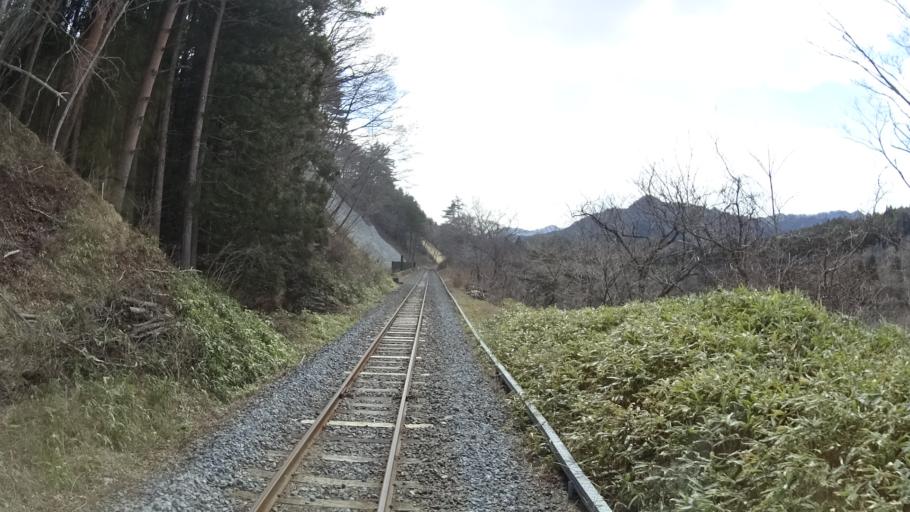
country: JP
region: Iwate
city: Yamada
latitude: 39.4853
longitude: 141.9253
